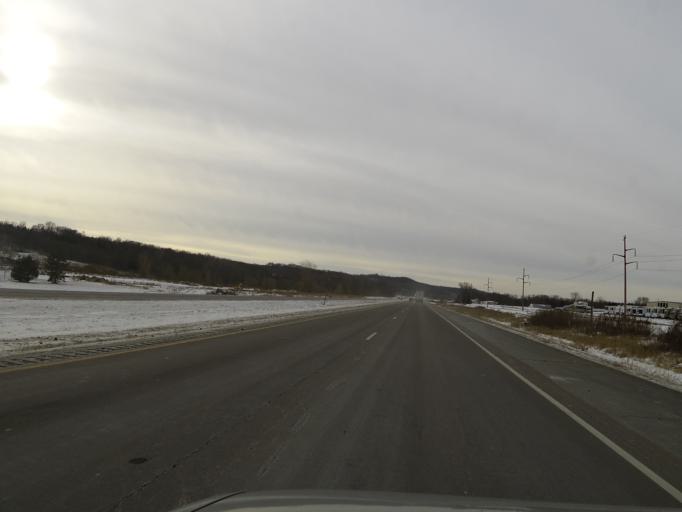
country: US
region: Minnesota
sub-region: Scott County
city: Jordan
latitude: 44.7078
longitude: -93.5927
